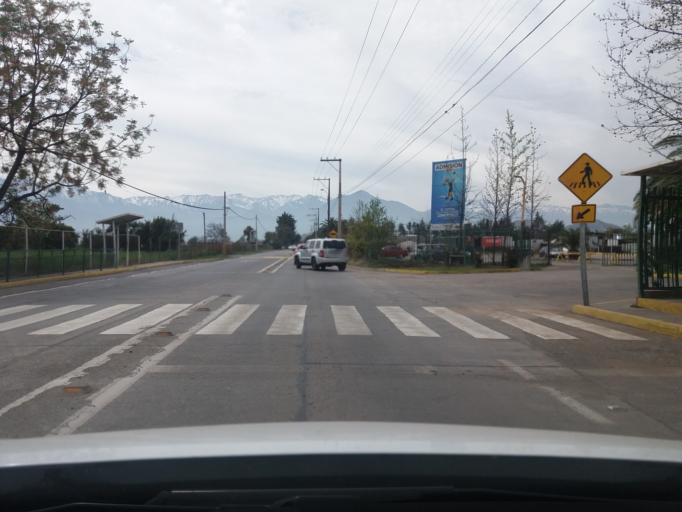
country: CL
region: Valparaiso
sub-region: Provincia de Los Andes
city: Los Andes
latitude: -32.8339
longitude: -70.6303
